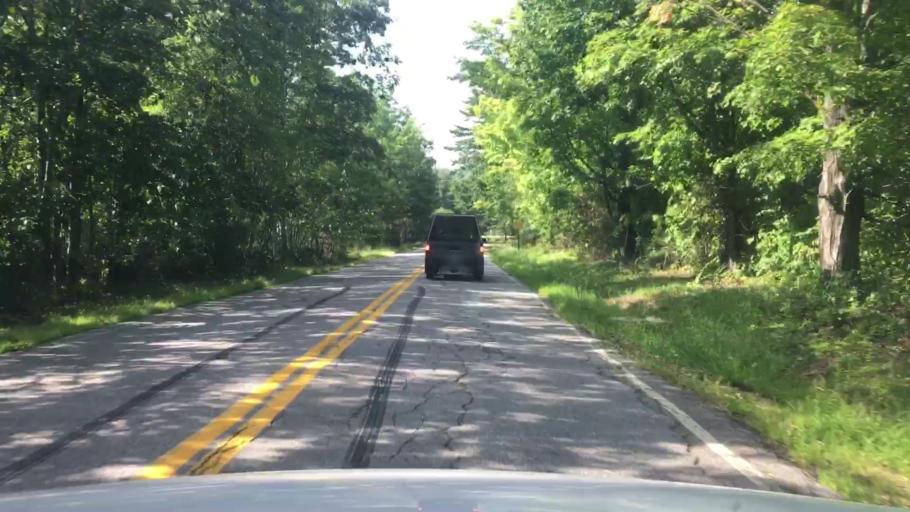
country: US
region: New Hampshire
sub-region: Belknap County
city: Gilford
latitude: 43.5635
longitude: -71.4143
